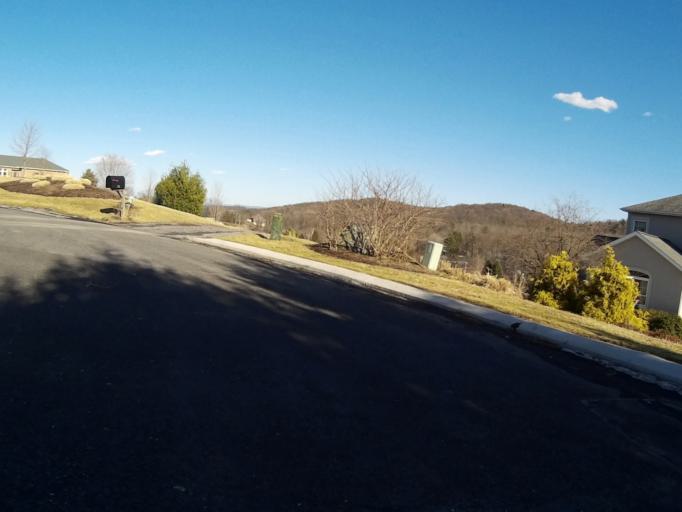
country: US
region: Pennsylvania
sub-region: Centre County
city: Park Forest Village
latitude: 40.8421
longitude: -77.9205
